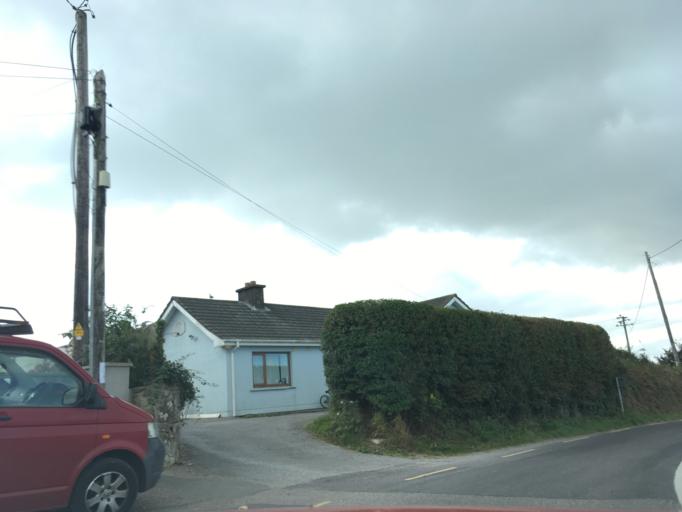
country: IE
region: Munster
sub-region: County Cork
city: Crosshaven
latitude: 51.7916
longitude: -8.2971
